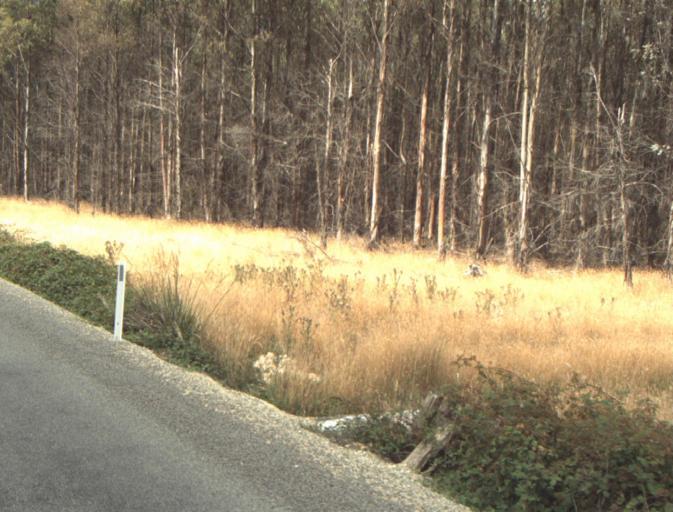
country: AU
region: Tasmania
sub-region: Launceston
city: Mayfield
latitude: -41.2134
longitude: 147.1901
